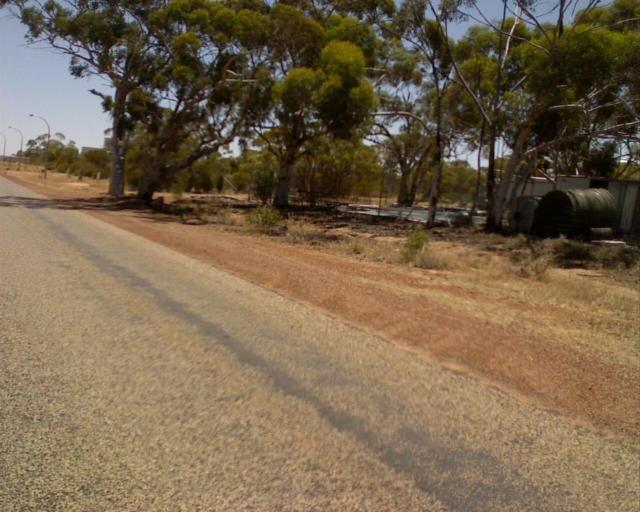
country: AU
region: Western Australia
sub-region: Merredin
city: Merredin
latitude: -30.8165
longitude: 117.8677
